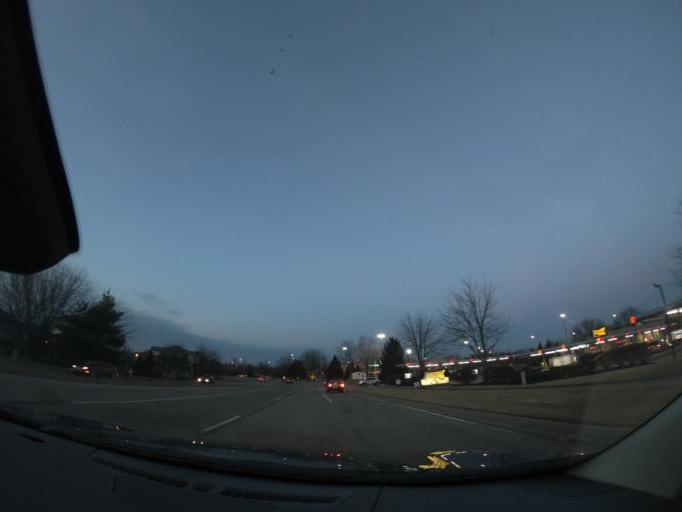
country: US
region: Kentucky
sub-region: Jefferson County
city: Worthington
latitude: 38.3000
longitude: -85.5598
